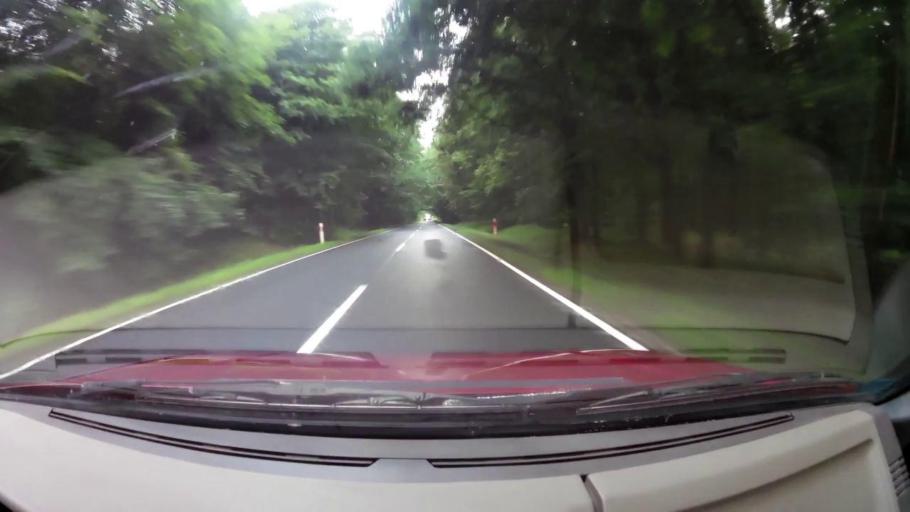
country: PL
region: West Pomeranian Voivodeship
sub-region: Powiat stargardzki
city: Chociwel
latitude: 53.4828
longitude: 15.3864
